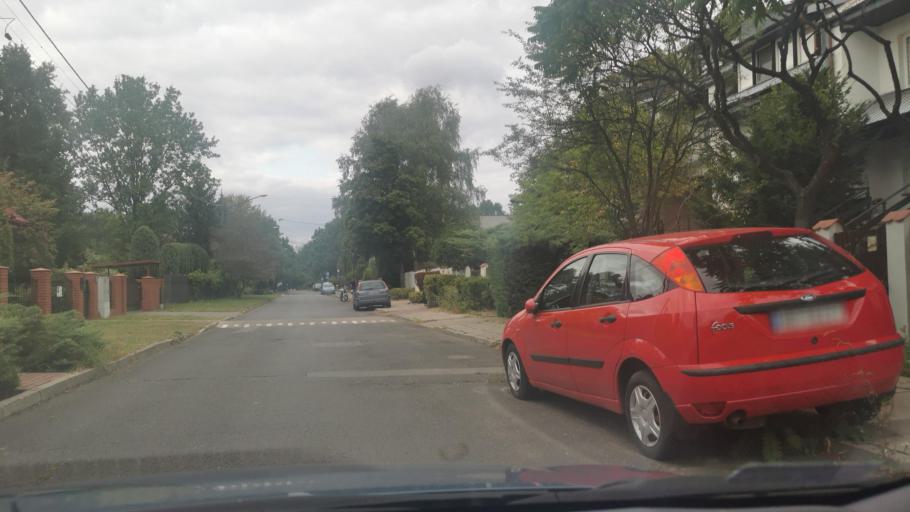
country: PL
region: Masovian Voivodeship
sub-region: Warszawa
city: Wawer
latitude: 52.2121
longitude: 21.1532
